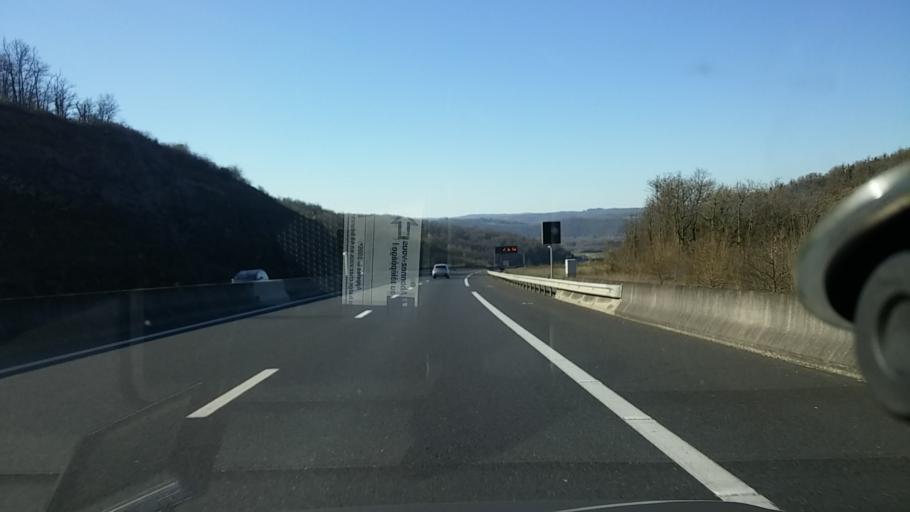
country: FR
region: Midi-Pyrenees
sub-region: Departement du Lot
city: Souillac
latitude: 44.8736
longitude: 1.5073
